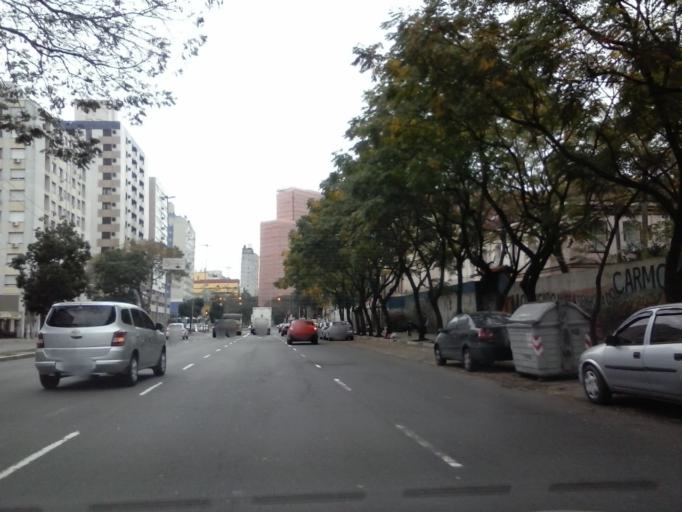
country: BR
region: Rio Grande do Sul
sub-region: Porto Alegre
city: Porto Alegre
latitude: -30.0365
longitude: -51.2253
